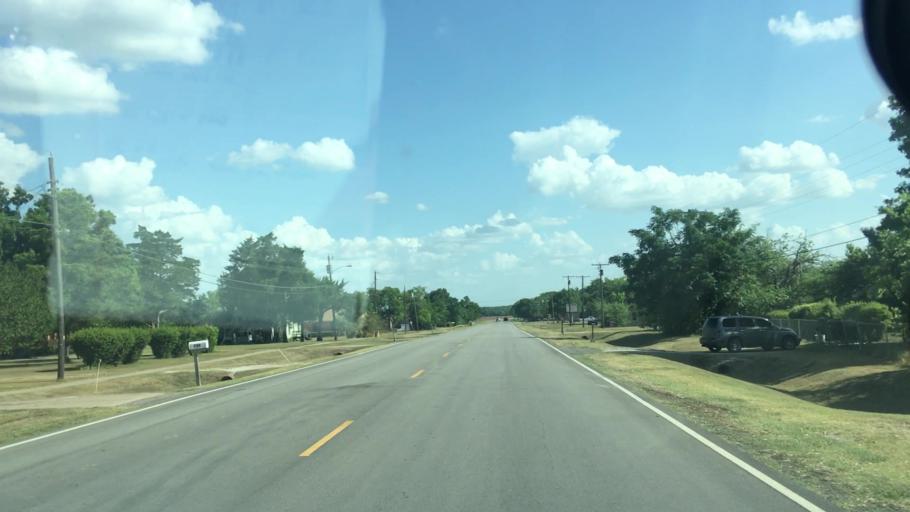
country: US
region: Texas
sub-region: Dallas County
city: Lancaster
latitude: 32.5994
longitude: -96.7479
